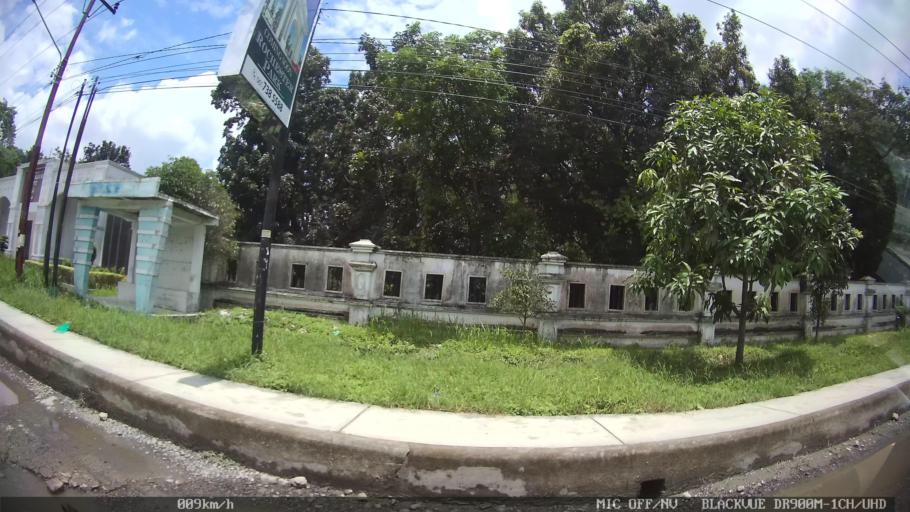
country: ID
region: North Sumatra
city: Medan
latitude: 3.6062
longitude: 98.7175
